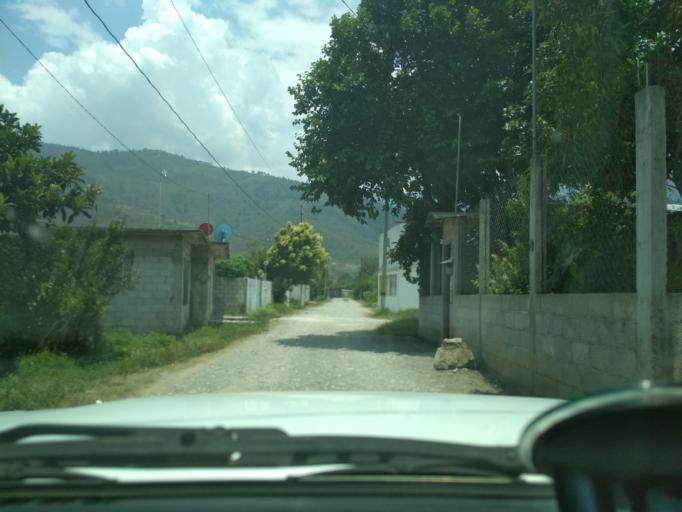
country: MX
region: Veracruz
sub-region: Acultzingo
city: Acatla
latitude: 18.7669
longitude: -97.2177
